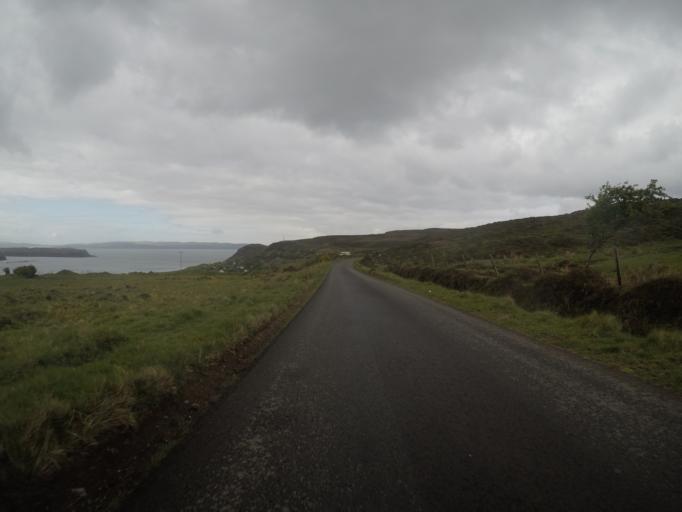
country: GB
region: Scotland
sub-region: Highland
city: Portree
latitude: 57.5939
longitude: -6.3682
